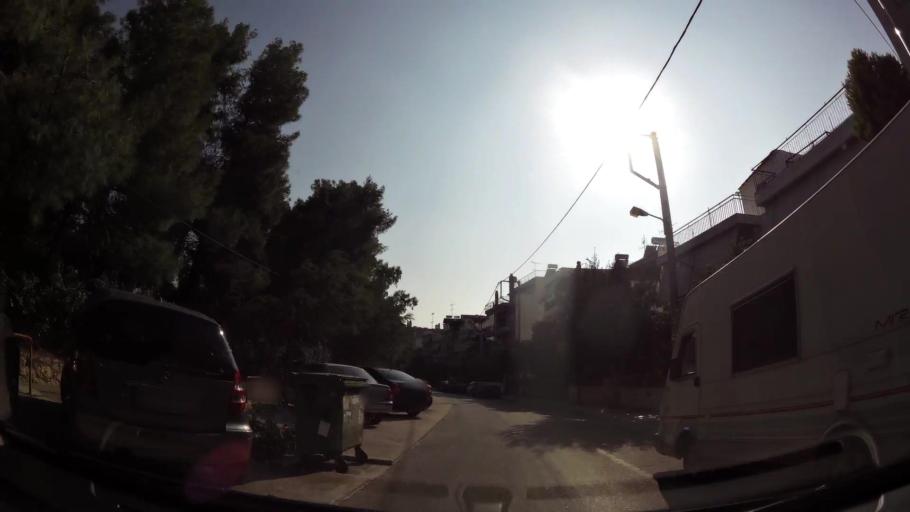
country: GR
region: Attica
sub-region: Nomarchia Athinas
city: Argyroupoli
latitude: 37.9035
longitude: 23.7569
